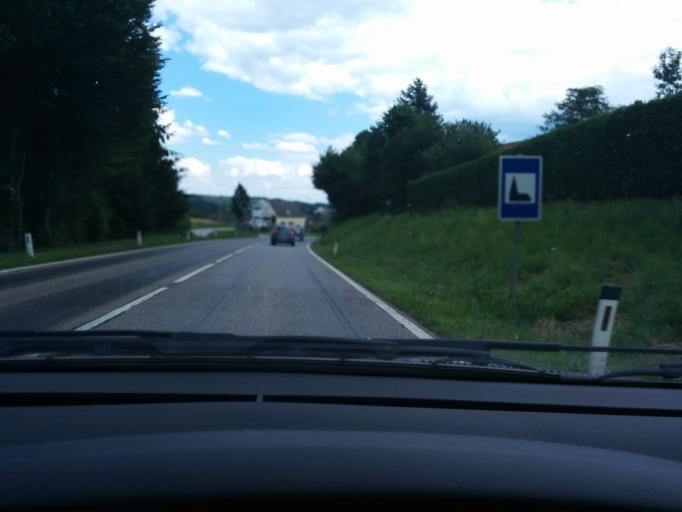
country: AT
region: Styria
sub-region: Politischer Bezirk Weiz
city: Oberrettenbach
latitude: 47.1730
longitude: 15.7955
